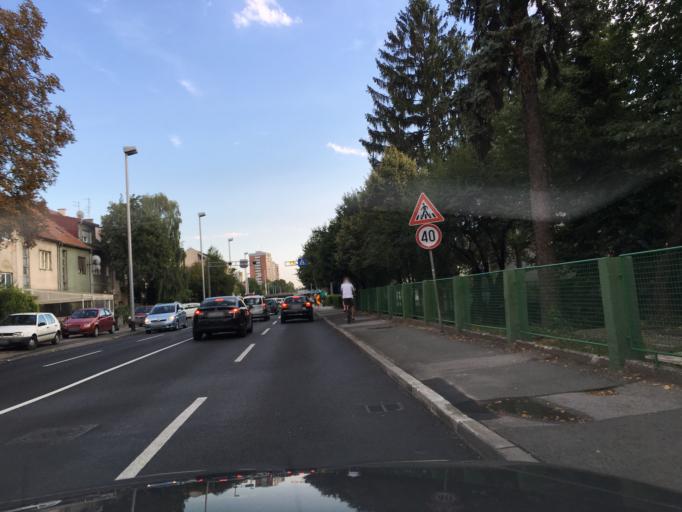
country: HR
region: Grad Zagreb
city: Zagreb - Centar
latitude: 45.7965
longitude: 15.9435
